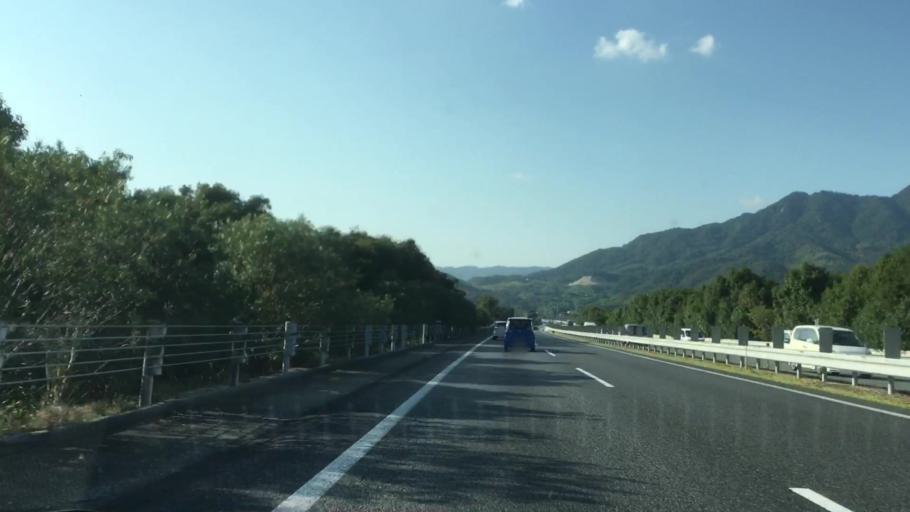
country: JP
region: Yamaguchi
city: Hofu
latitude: 34.0623
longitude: 131.6084
